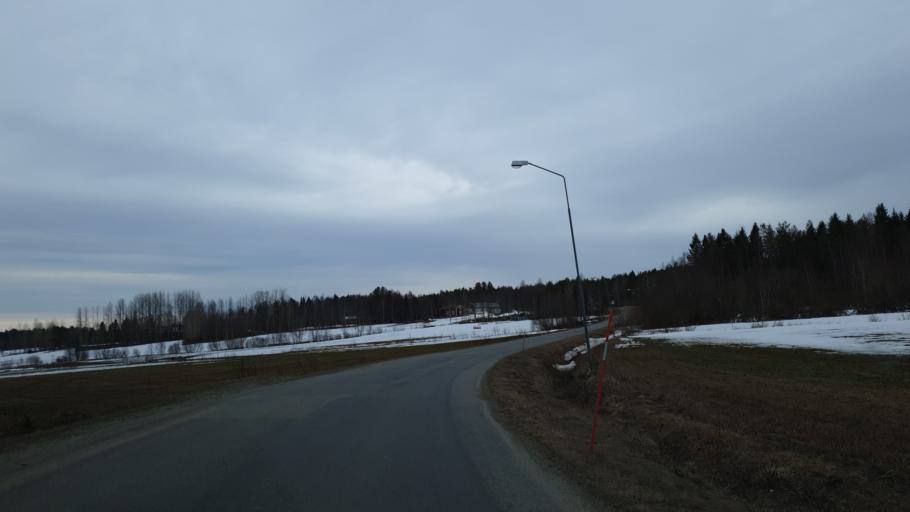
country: SE
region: Vaesterbotten
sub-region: Robertsfors Kommun
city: Robertsfors
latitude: 64.3982
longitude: 21.0034
